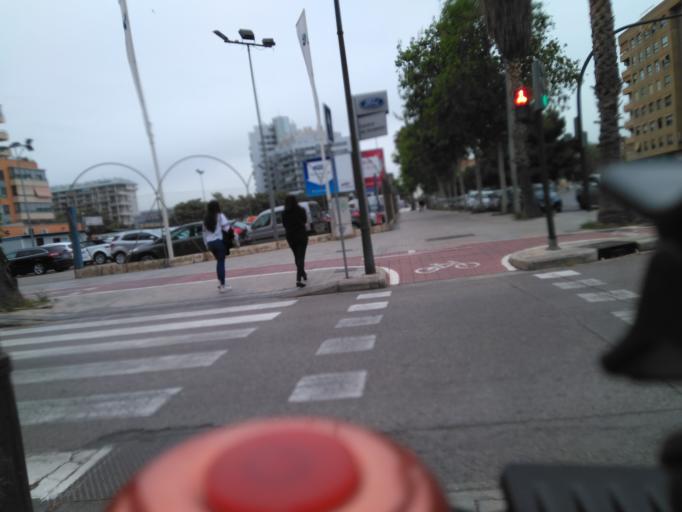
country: ES
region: Valencia
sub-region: Provincia de Valencia
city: Mislata
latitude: 39.4805
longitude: -0.4001
